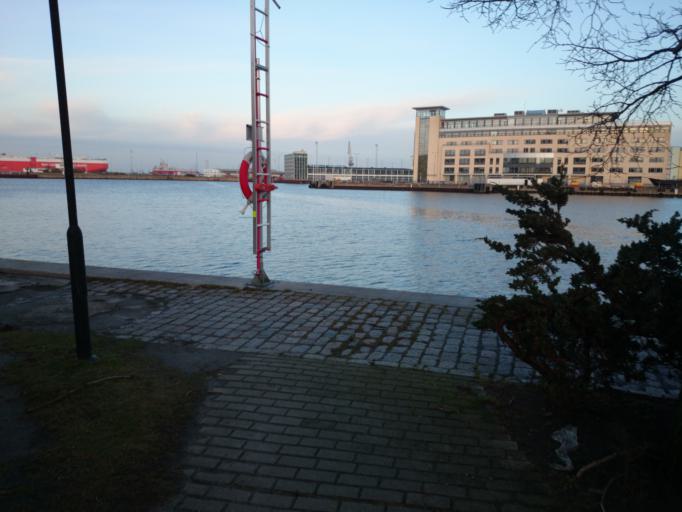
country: SE
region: Skane
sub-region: Malmo
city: Malmoe
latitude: 55.6129
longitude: 12.9935
